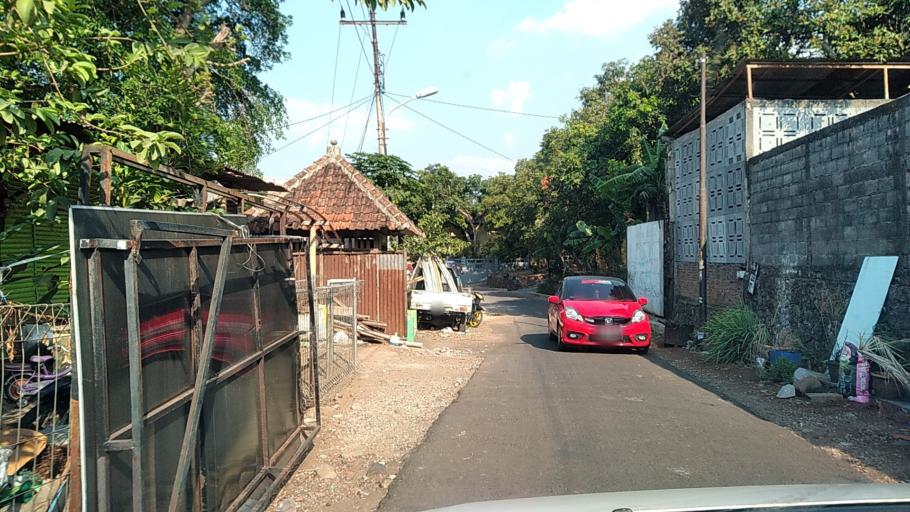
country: ID
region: Central Java
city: Semarang
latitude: -7.0658
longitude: 110.4262
